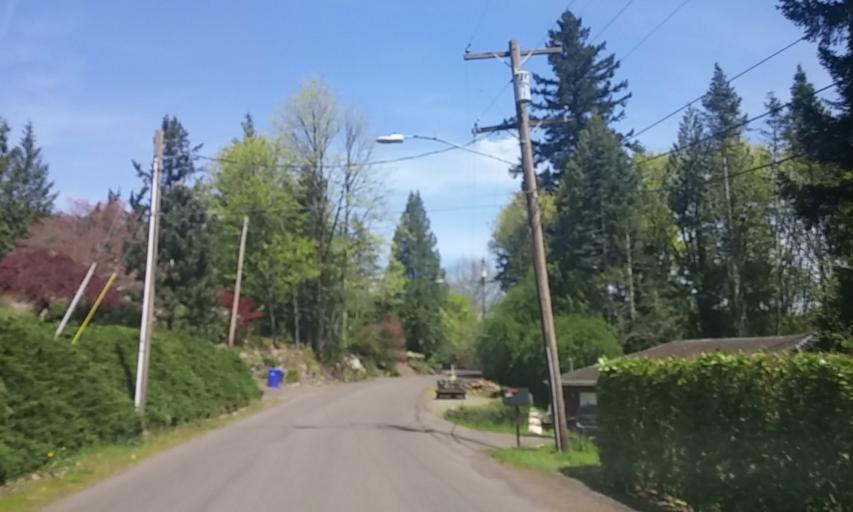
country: US
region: Oregon
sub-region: Washington County
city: West Slope
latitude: 45.5026
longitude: -122.7462
